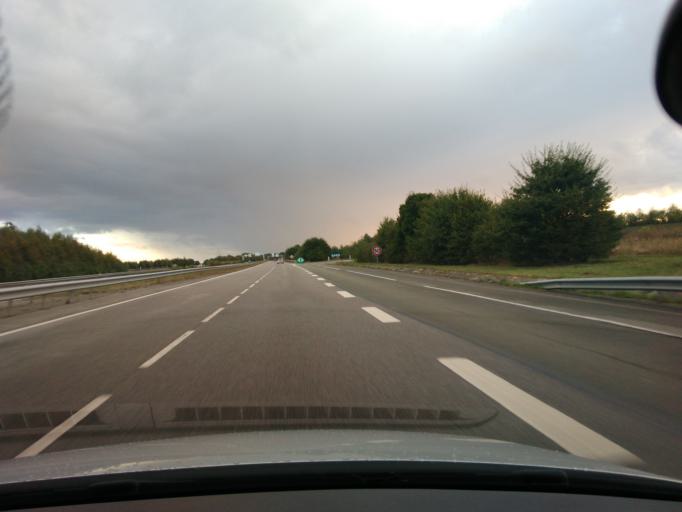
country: FR
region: Haute-Normandie
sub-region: Departement de l'Eure
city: Evreux
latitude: 49.0072
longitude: 1.1873
